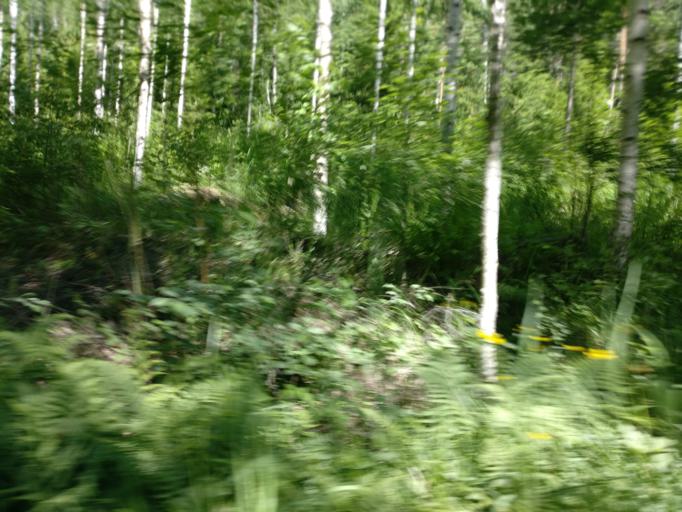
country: FI
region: Northern Savo
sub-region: Varkaus
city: Kangaslampi
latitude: 62.1748
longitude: 28.2395
